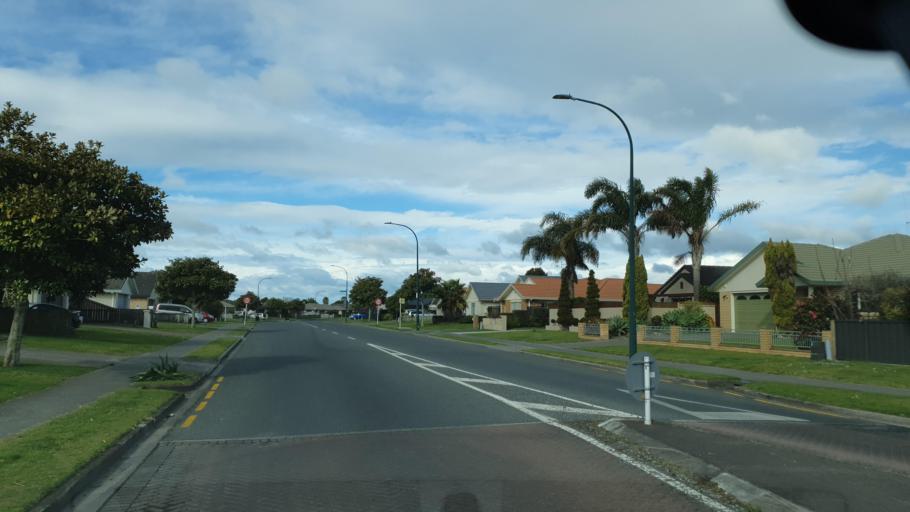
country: NZ
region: Bay of Plenty
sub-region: Tauranga City
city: Tauranga
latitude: -37.6952
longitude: 176.2594
